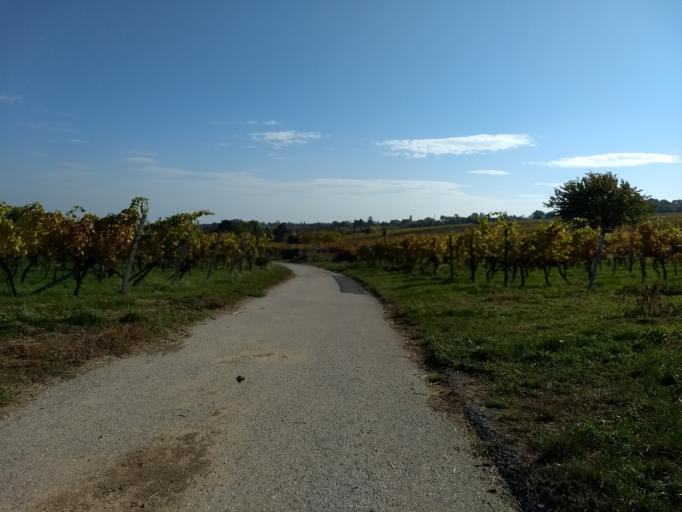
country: AT
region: Lower Austria
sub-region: Politischer Bezirk Modling
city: Giesshubl
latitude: 48.1103
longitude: 16.2421
